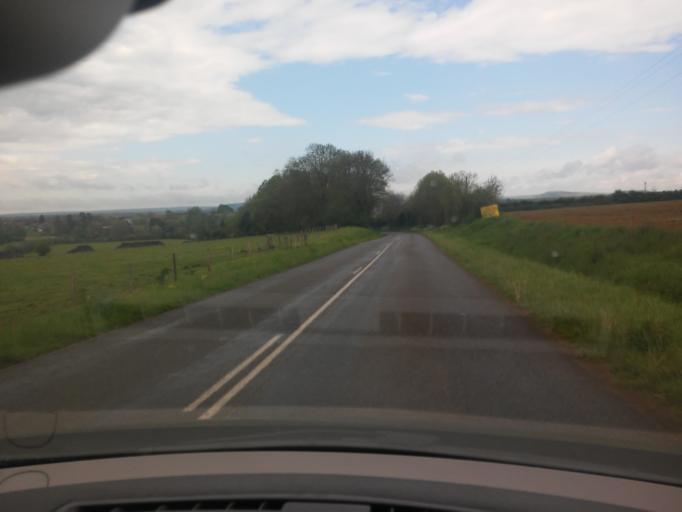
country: FR
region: Lorraine
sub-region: Departement de Meurthe-et-Moselle
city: Longuyon
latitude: 49.3605
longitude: 5.5364
